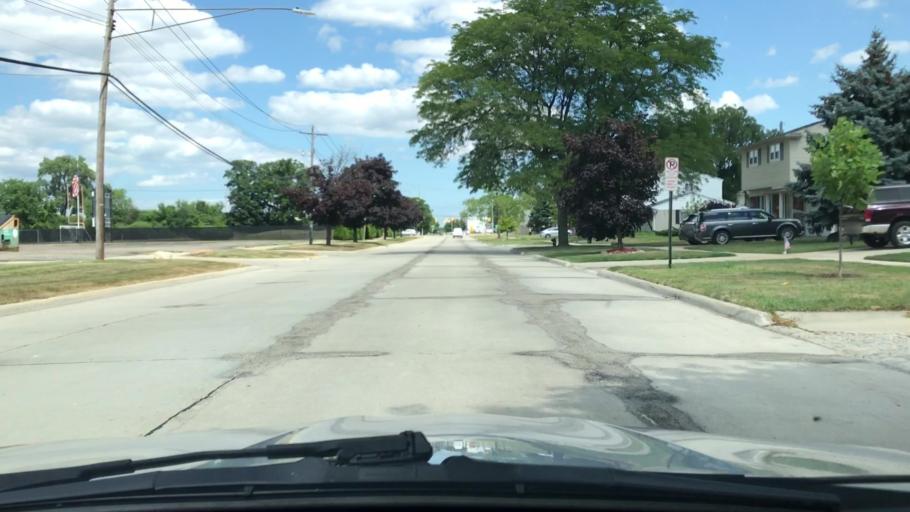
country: US
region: Michigan
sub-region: Oakland County
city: Clawson
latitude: 42.5276
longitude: -83.1236
